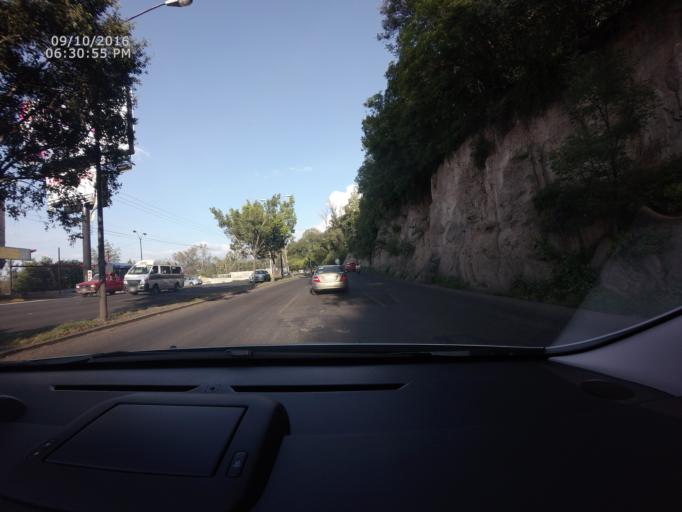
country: MX
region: Michoacan
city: Morelia
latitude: 19.6811
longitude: -101.1983
